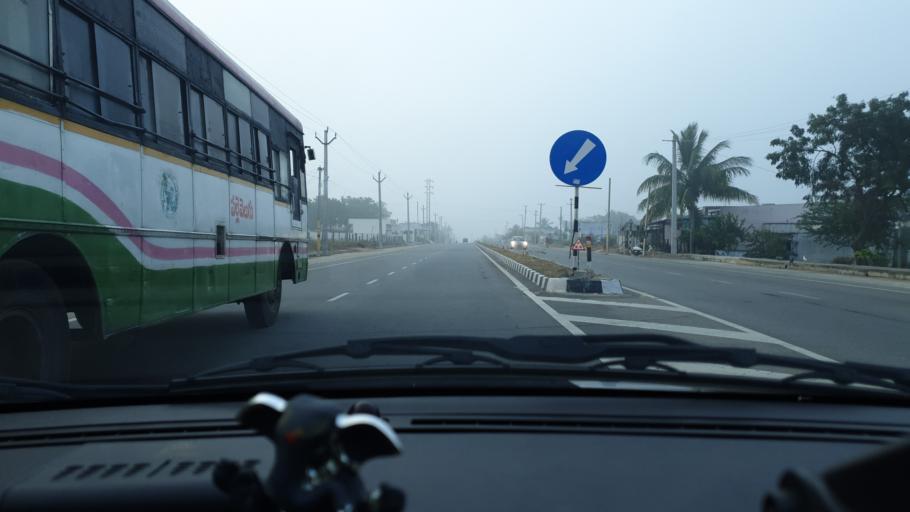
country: IN
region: Telangana
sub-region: Mahbubnagar
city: Farrukhnagar
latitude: 16.8851
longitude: 78.5290
